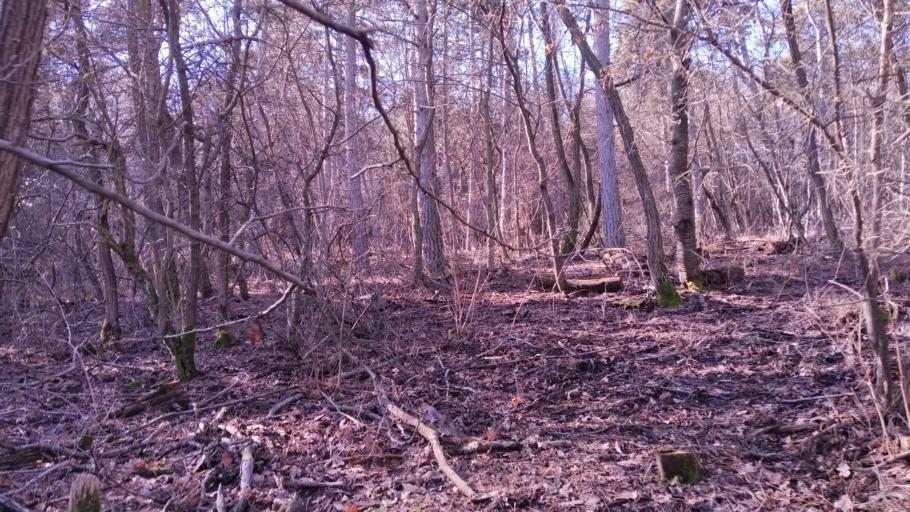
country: HU
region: Pest
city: Urom
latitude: 47.6090
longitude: 19.0119
